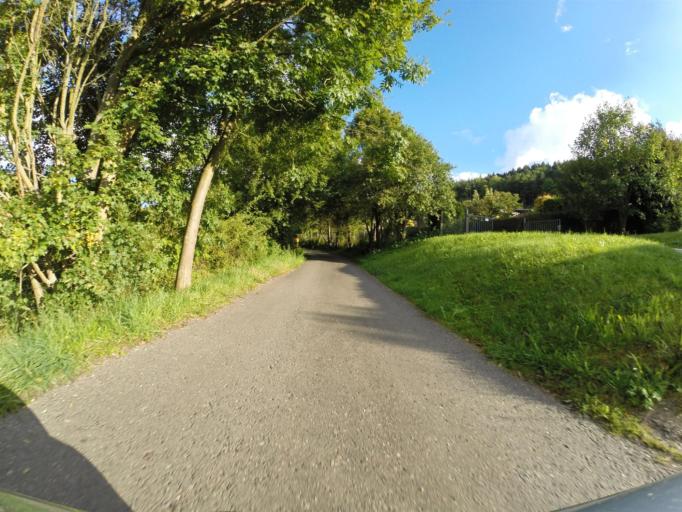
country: DE
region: Thuringia
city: Sulza
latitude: 50.8863
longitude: 11.5809
